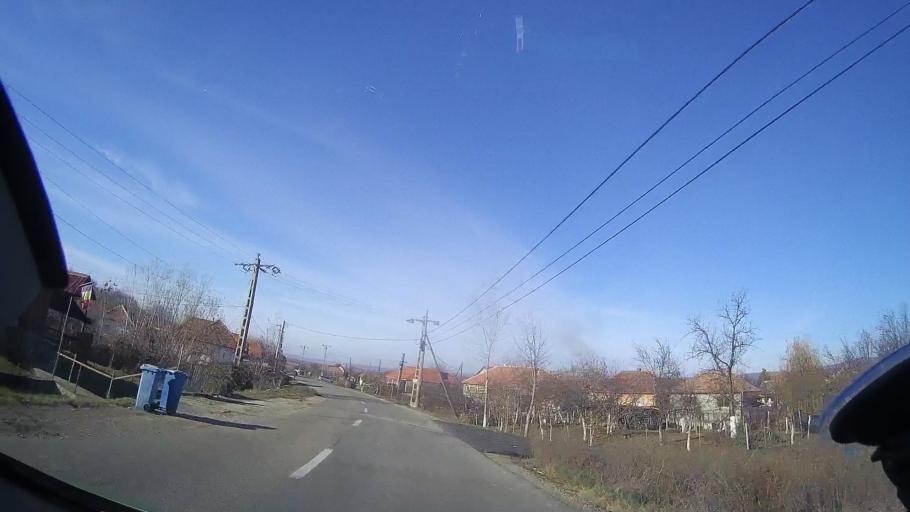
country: RO
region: Bihor
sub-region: Comuna Vadu Crisului
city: Vadu Crisului
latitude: 46.9880
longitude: 22.5282
